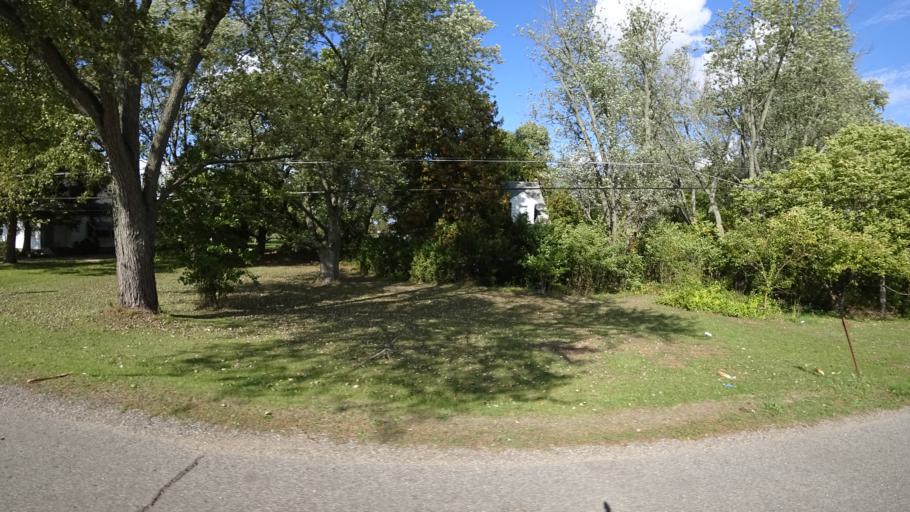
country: US
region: Michigan
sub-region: Saint Joseph County
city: Three Rivers
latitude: 41.9548
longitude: -85.6158
